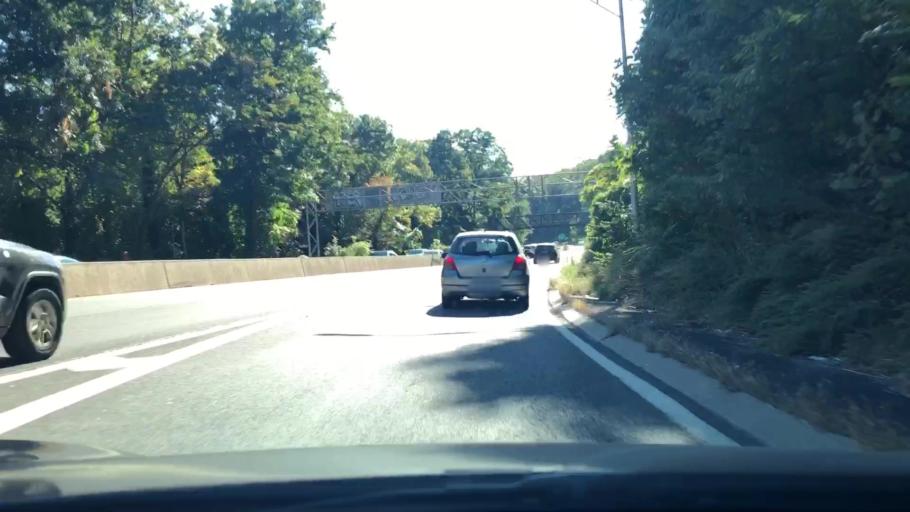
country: US
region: New York
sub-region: Westchester County
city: Yonkers
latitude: 40.9282
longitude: -73.8792
